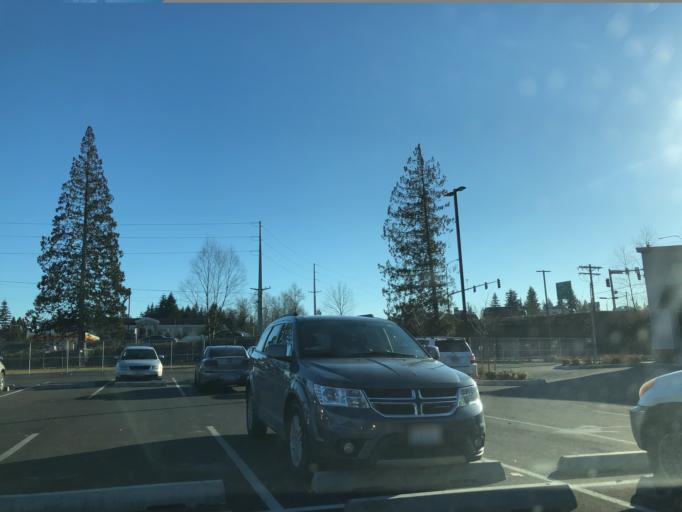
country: US
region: Washington
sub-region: Snohomish County
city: Marysville
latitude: 48.0765
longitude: -122.1831
